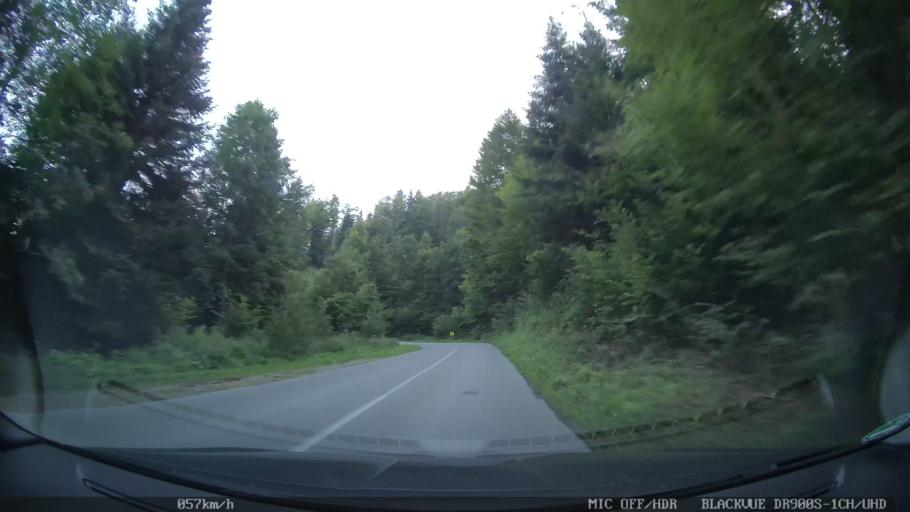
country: HR
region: Primorsko-Goranska
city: Vrbovsko
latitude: 45.2082
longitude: 15.0293
